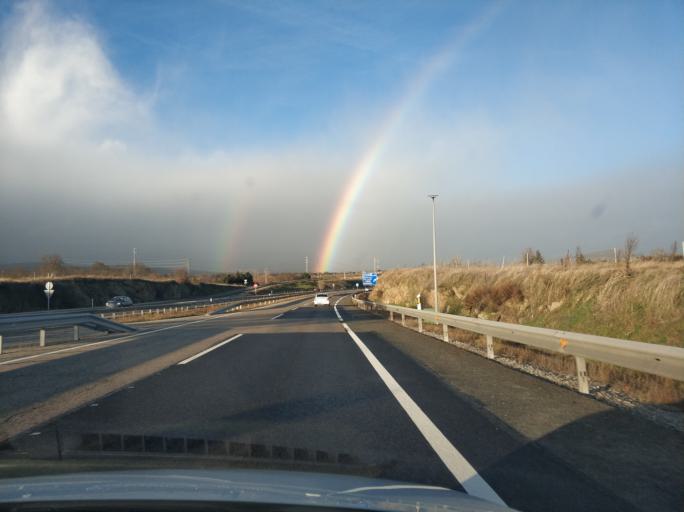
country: ES
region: Madrid
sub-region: Provincia de Madrid
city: Buitrago del Lozoya
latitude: 40.9955
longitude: -3.6417
